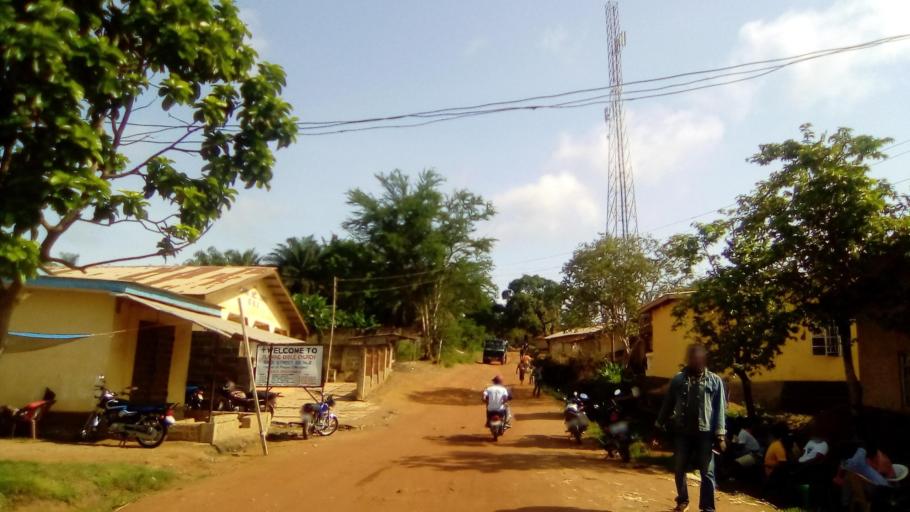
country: SL
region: Southern Province
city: Bo
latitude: 7.9704
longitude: -11.7310
